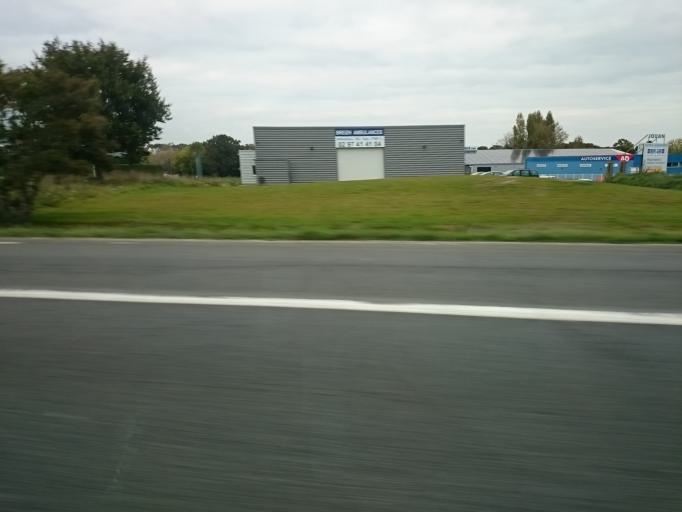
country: FR
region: Brittany
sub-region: Departement du Morbihan
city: Muzillac
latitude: 47.5606
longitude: -2.5030
